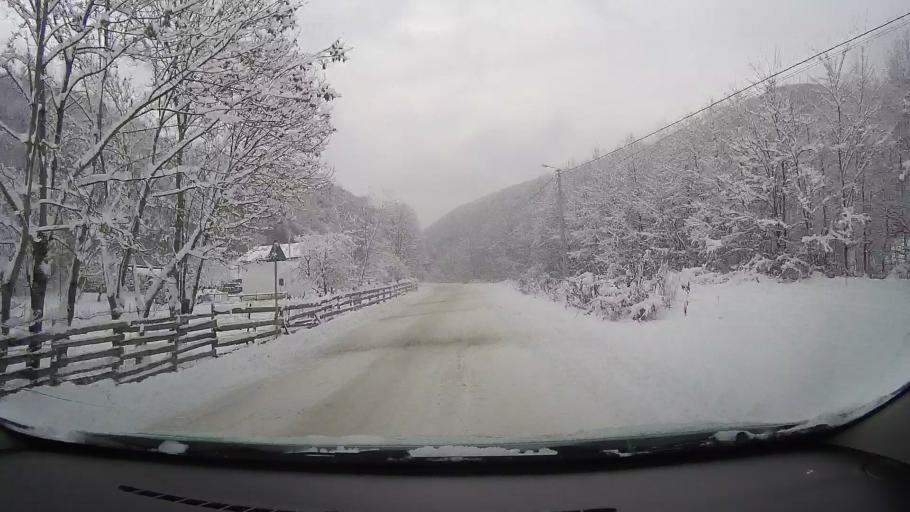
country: RO
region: Alba
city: Pianu de Sus
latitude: 45.8778
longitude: 23.4921
